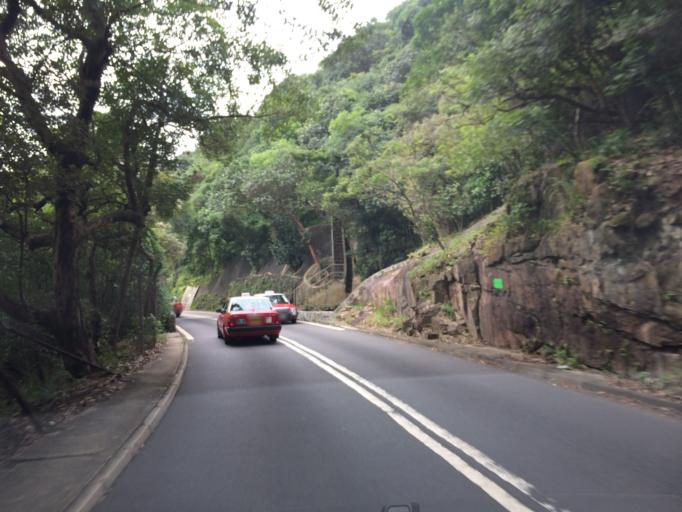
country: HK
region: Wanchai
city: Wan Chai
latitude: 22.2617
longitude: 114.2256
